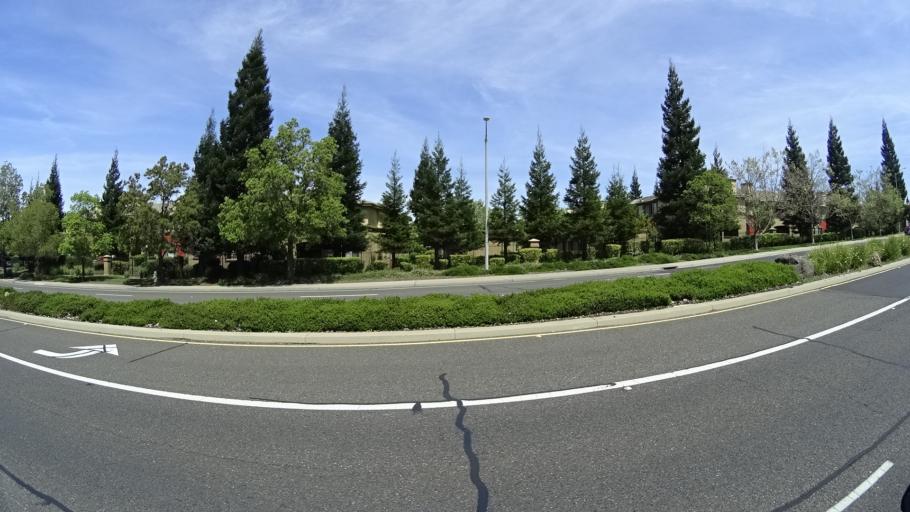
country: US
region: California
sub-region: Placer County
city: Rocklin
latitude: 38.8089
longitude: -121.2810
